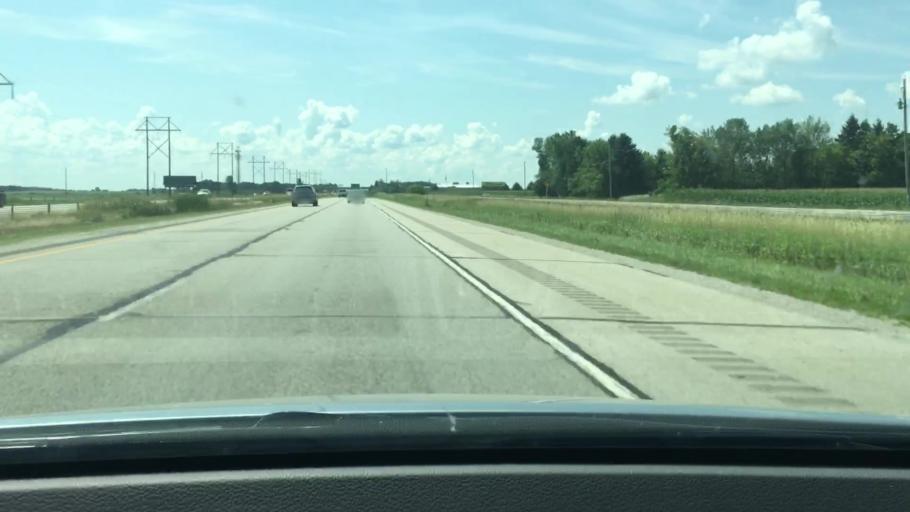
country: US
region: Wisconsin
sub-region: Winnebago County
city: Oshkosh
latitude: 43.9172
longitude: -88.5837
